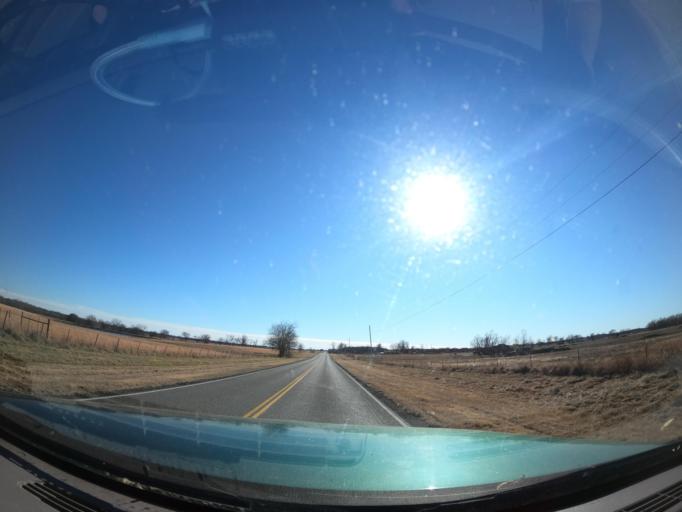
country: US
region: Oklahoma
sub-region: Muskogee County
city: Haskell
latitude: 35.6845
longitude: -95.6423
